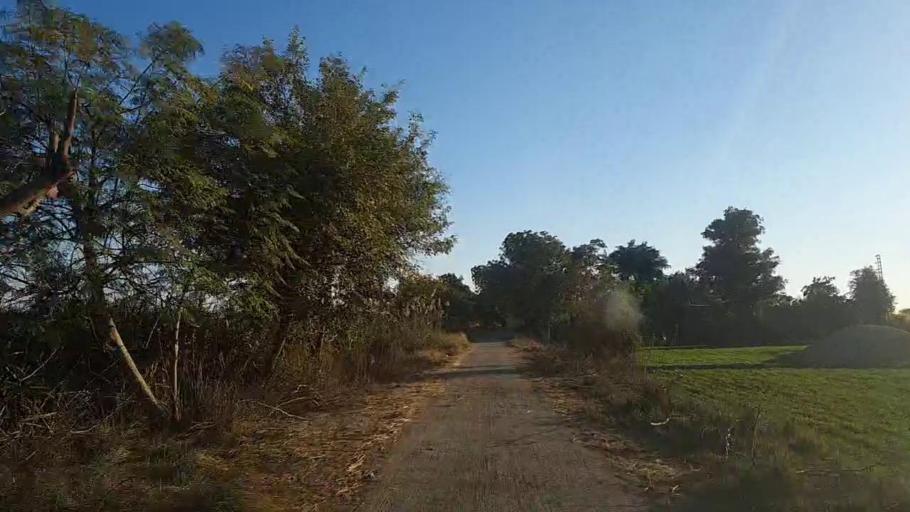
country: PK
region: Sindh
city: Sanghar
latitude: 26.1386
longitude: 68.9436
